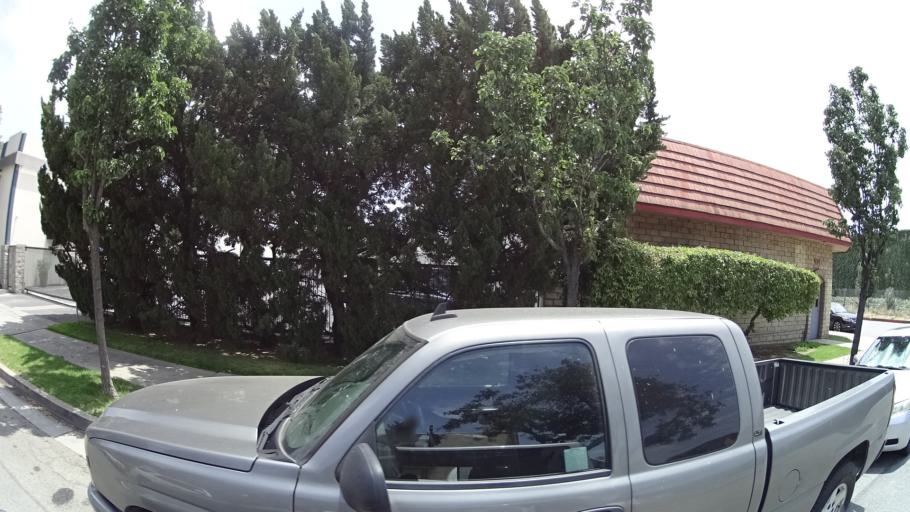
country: US
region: California
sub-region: Los Angeles County
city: Burbank
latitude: 34.1642
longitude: -118.2944
